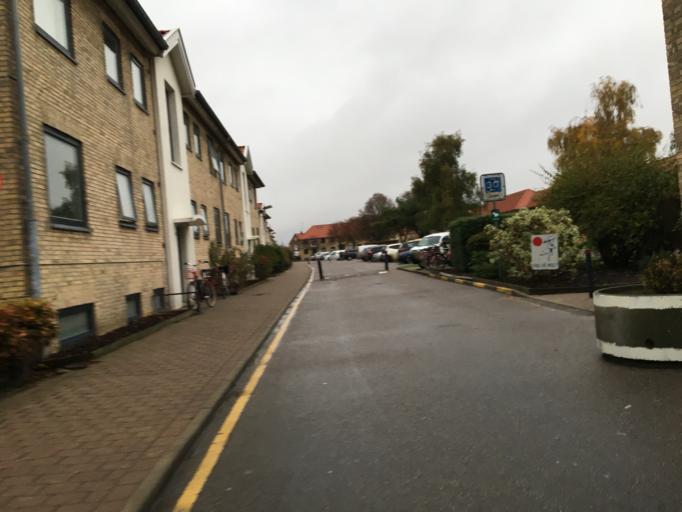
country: DK
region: Capital Region
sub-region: Tarnby Kommune
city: Tarnby
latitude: 55.6345
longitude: 12.6292
